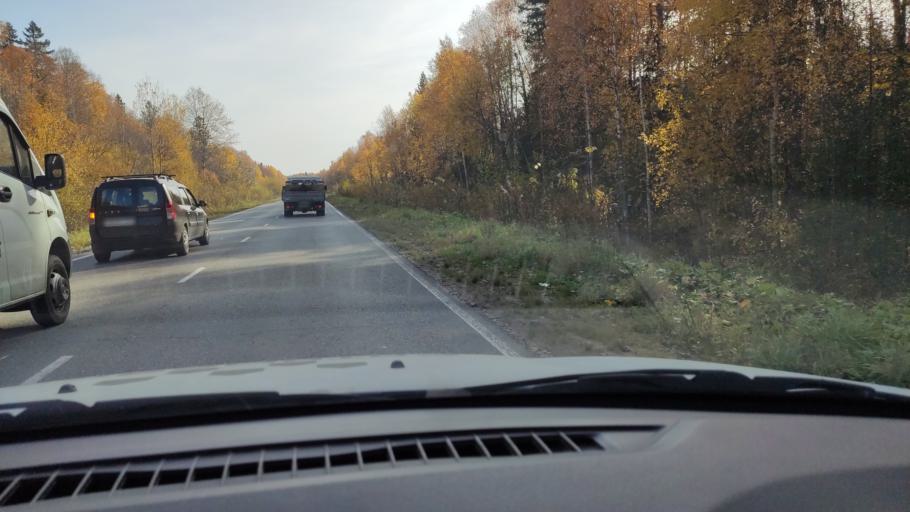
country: RU
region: Perm
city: Novyye Lyady
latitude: 58.0249
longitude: 56.6354
